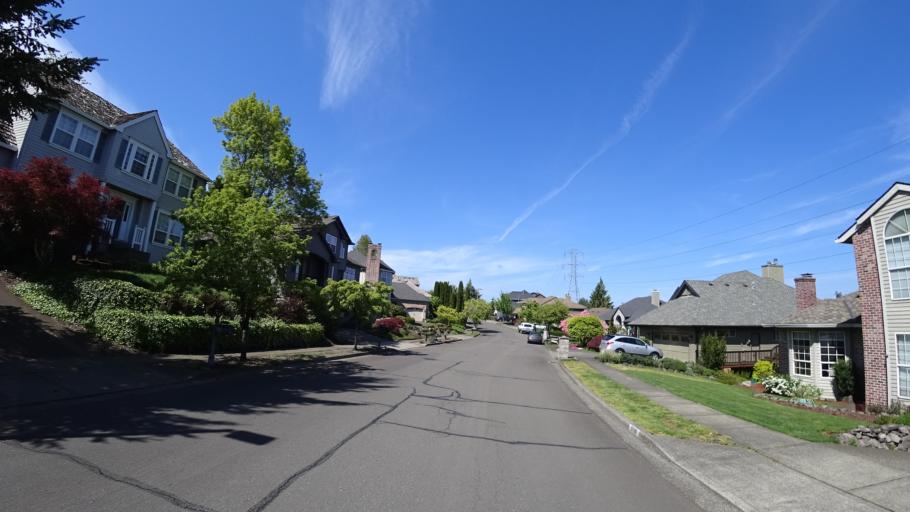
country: US
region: Oregon
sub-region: Washington County
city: Aloha
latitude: 45.4491
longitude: -122.8422
